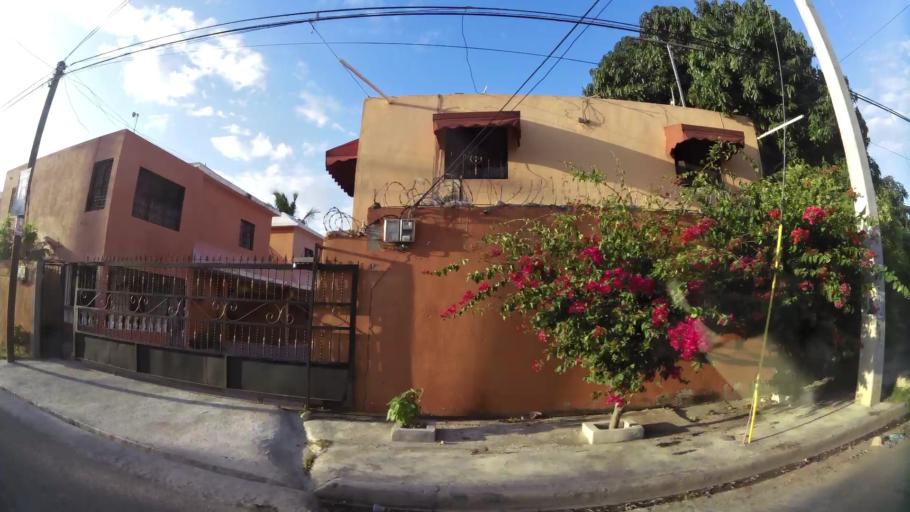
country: DO
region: Santo Domingo
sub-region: Santo Domingo
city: Santo Domingo Este
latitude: 18.4821
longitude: -69.8322
